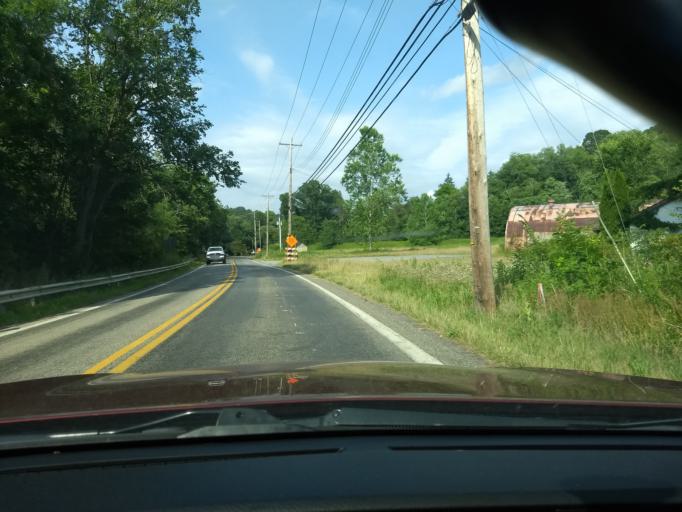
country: US
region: Pennsylvania
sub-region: Allegheny County
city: Bell Acres
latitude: 40.6063
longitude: -80.1650
